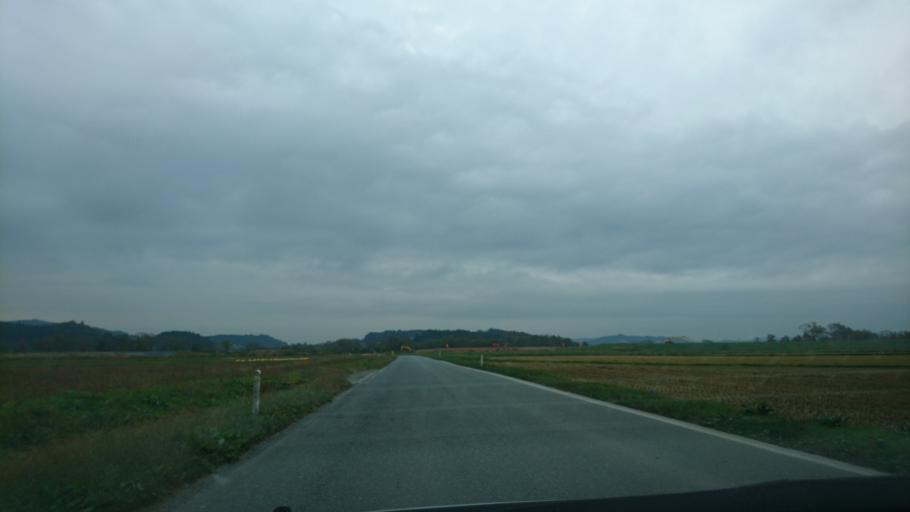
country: JP
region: Iwate
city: Ichinoseki
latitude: 38.9543
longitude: 141.1689
